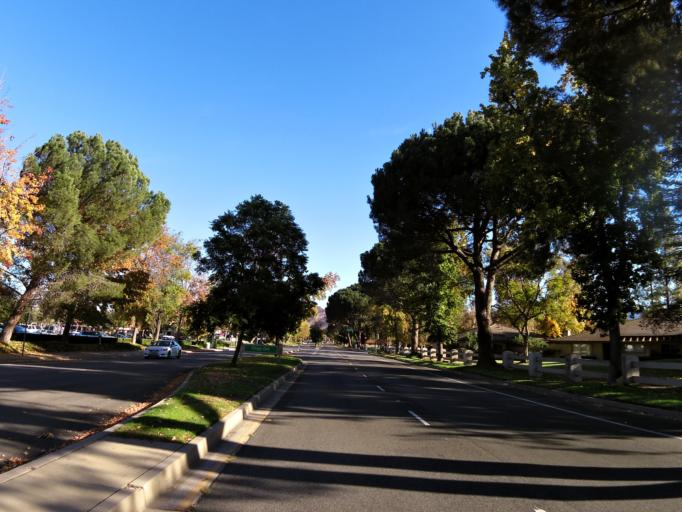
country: US
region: California
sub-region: Los Angeles County
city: Westlake Village
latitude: 34.1510
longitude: -118.8266
